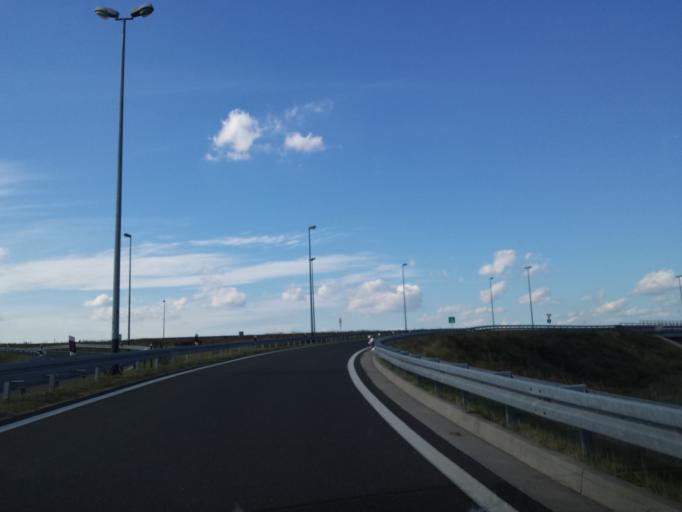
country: HR
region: Zagrebacka
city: Gradici
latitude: 45.6903
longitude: 16.0691
